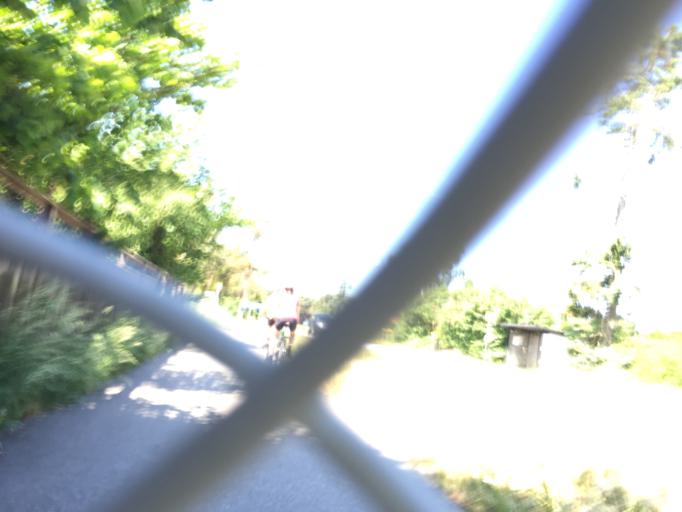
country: SE
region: Skane
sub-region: Trelleborgs Kommun
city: Anderslov
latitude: 55.3457
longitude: 13.2811
